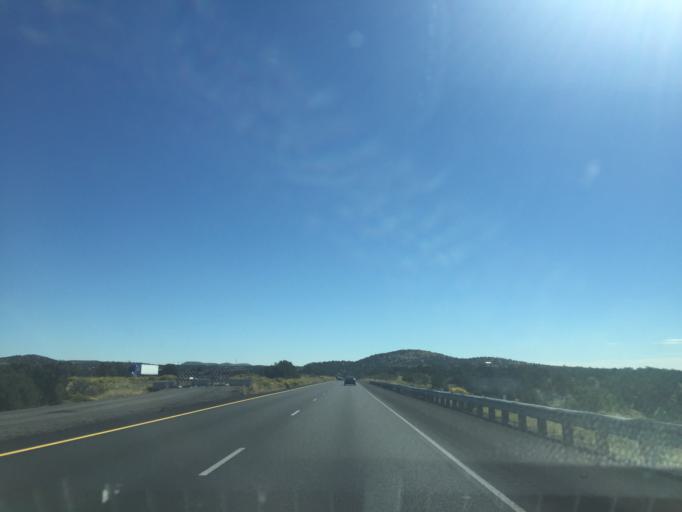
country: US
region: Arizona
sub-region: Coconino County
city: Flagstaff
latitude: 35.2015
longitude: -111.4363
